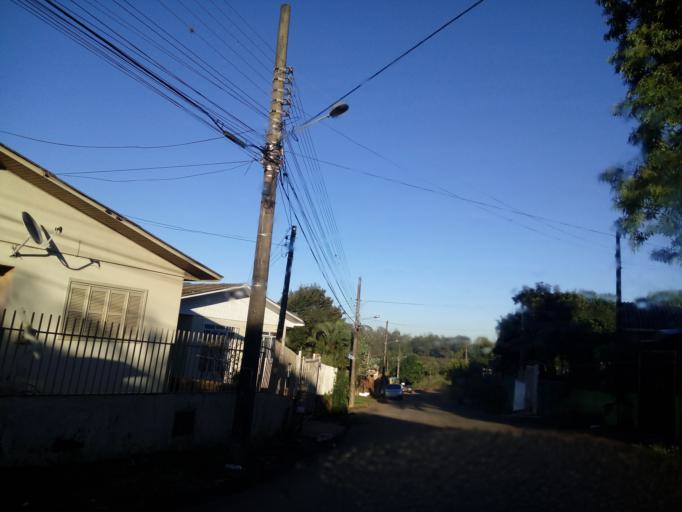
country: BR
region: Santa Catarina
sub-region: Chapeco
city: Chapeco
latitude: -27.1246
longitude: -52.6202
